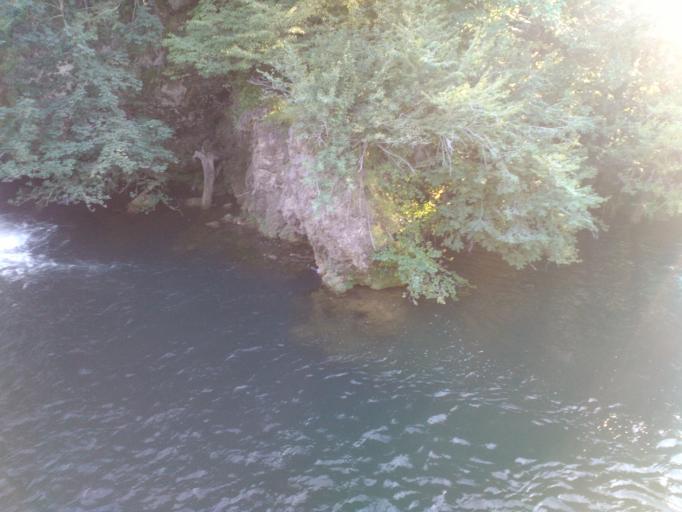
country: BA
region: Federation of Bosnia and Herzegovina
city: Orasac
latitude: 44.4876
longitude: 16.1427
